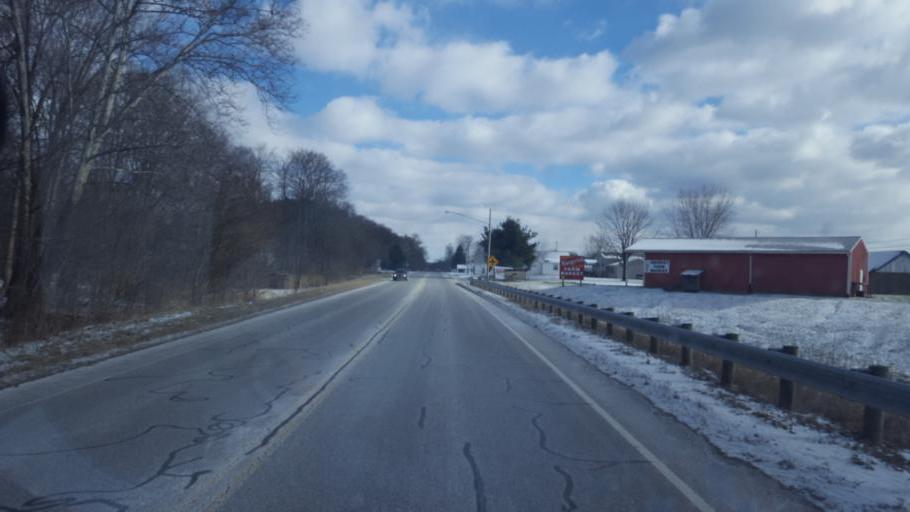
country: US
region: Ohio
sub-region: Muskingum County
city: Dresden
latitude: 40.1559
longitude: -81.9505
